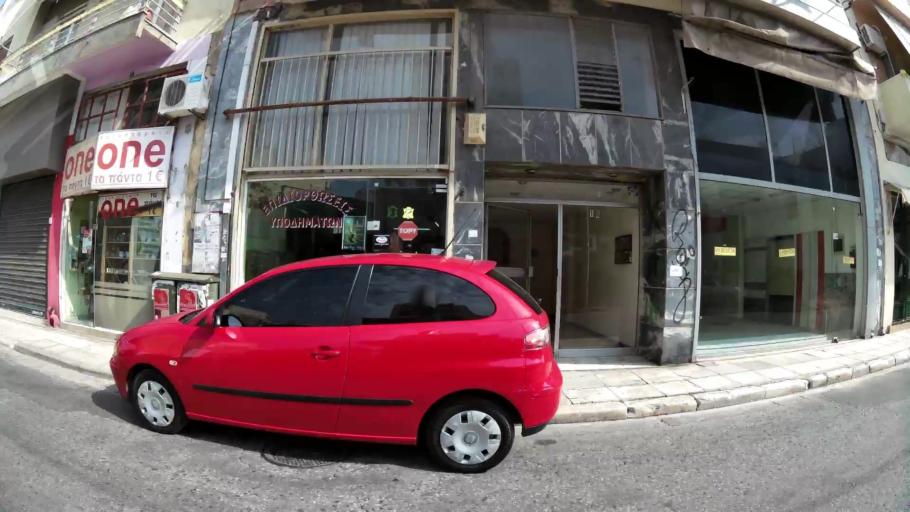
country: GR
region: Attica
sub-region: Nomarchia Athinas
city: Athens
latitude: 37.9908
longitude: 23.7110
